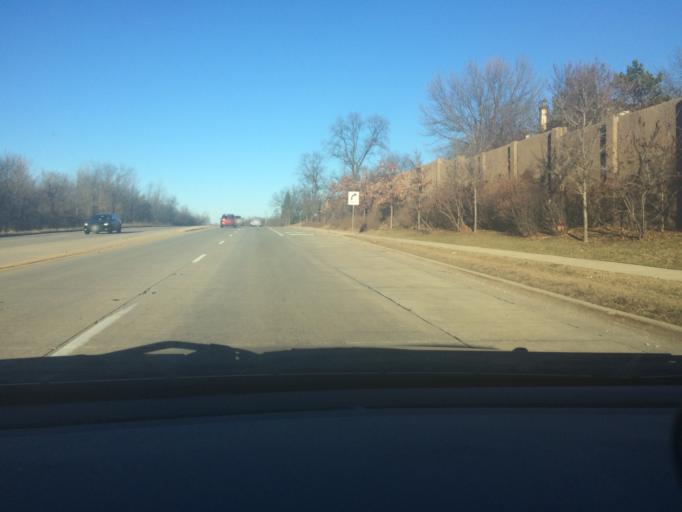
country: US
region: Illinois
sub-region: Cook County
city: Streamwood
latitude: 42.0382
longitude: -88.1968
